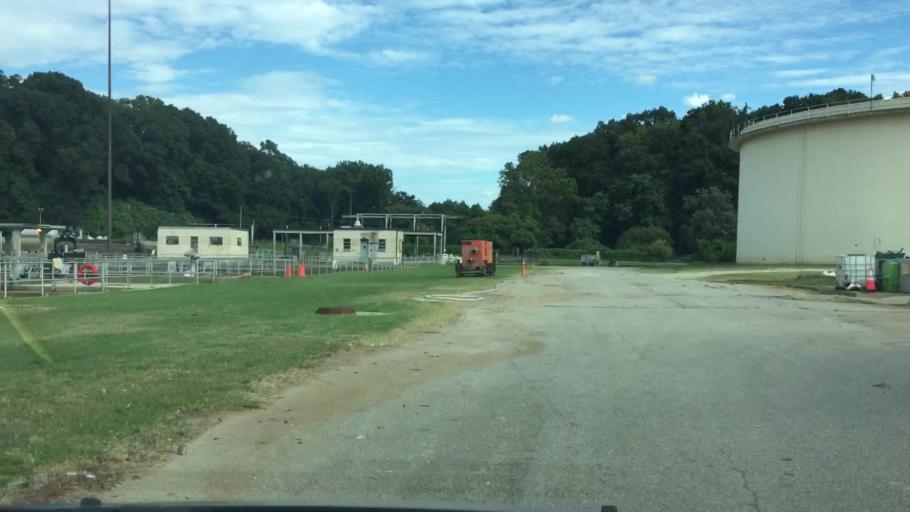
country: US
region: Georgia
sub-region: DeKalb County
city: Gresham Park
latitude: 33.7031
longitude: -84.3350
